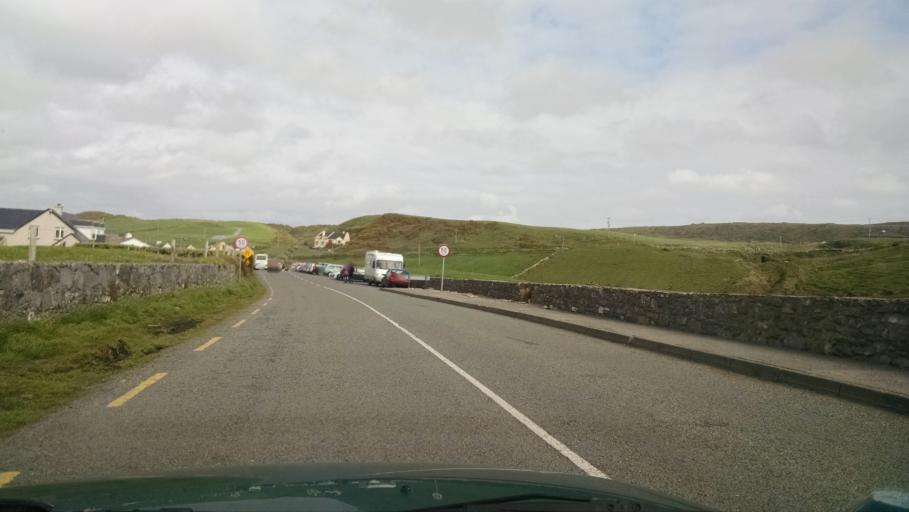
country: IE
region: Connaught
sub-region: County Galway
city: Bearna
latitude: 53.0123
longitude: -9.3904
